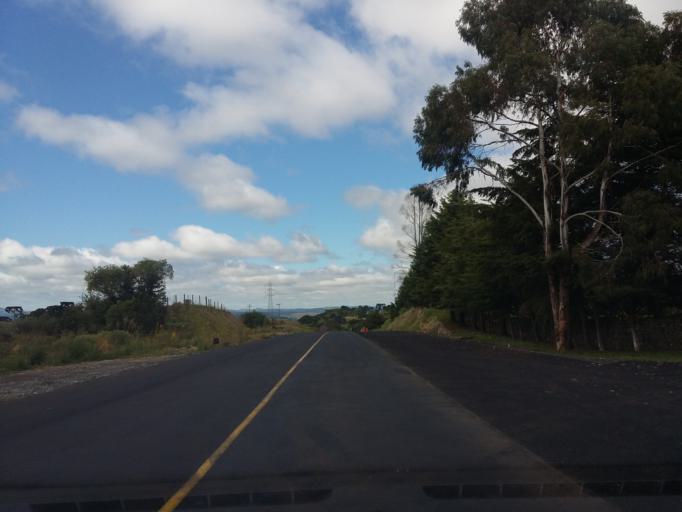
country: BR
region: Santa Catarina
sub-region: Sao Joaquim
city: Sao Joaquim
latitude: -28.0536
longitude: -50.0737
